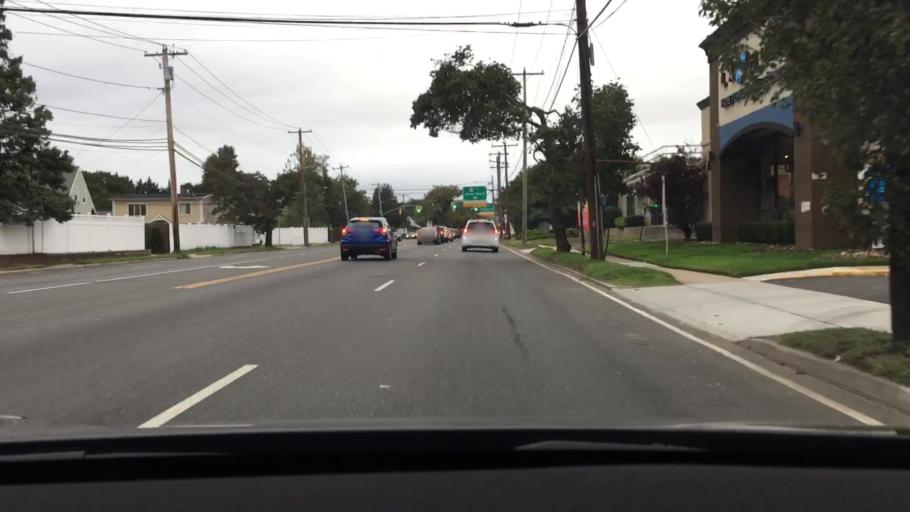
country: US
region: New York
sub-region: Nassau County
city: Carle Place
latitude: 40.7510
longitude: -73.6183
